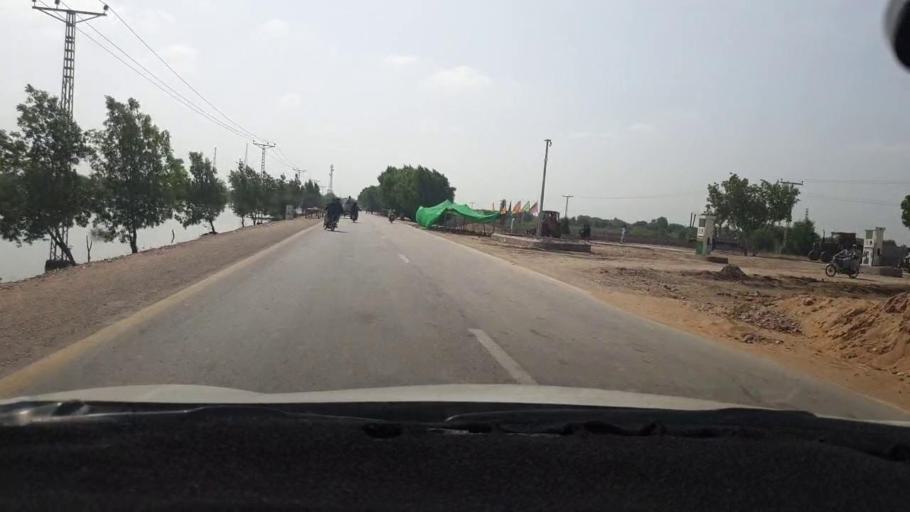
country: PK
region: Sindh
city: Mirpur Khas
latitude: 25.7150
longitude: 69.1227
